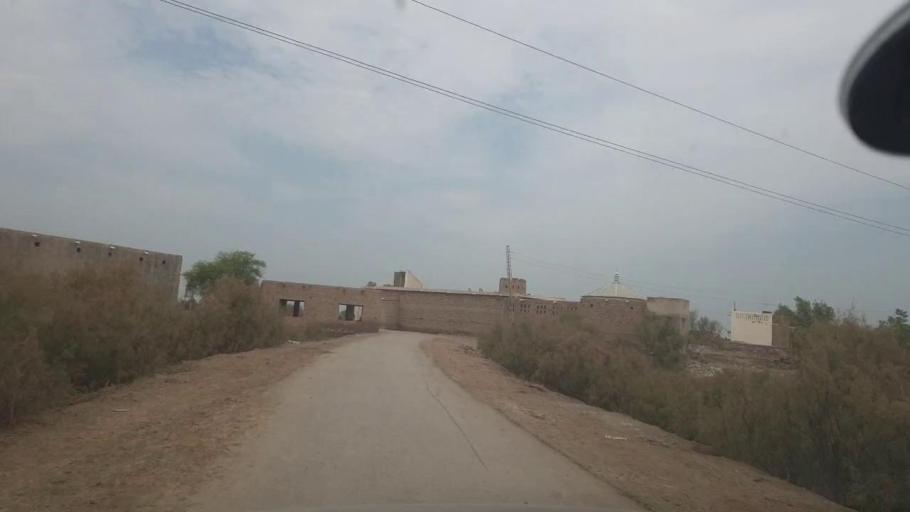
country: PK
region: Balochistan
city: Mehrabpur
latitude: 28.0589
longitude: 68.1510
